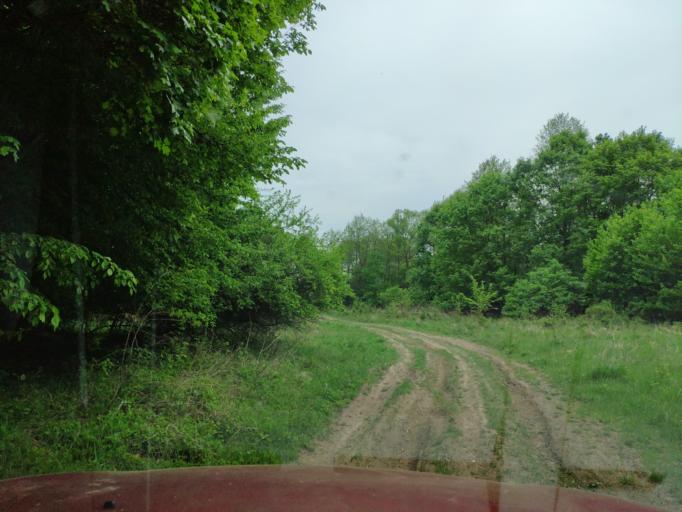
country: SK
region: Banskobystricky
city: Revuca
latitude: 48.5172
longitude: 20.1637
